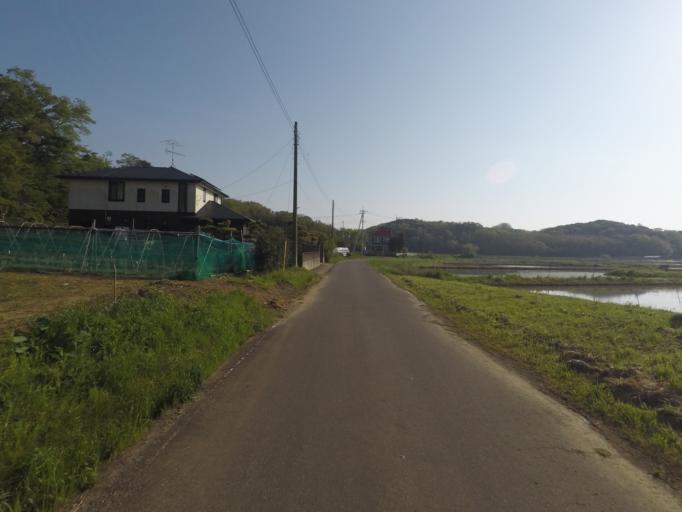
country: JP
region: Ibaraki
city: Inashiki
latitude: 36.0689
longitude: 140.3600
